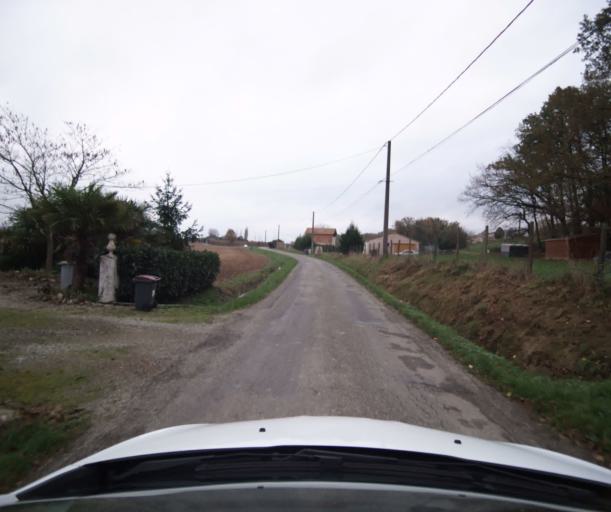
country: FR
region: Midi-Pyrenees
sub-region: Departement du Tarn-et-Garonne
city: Moissac
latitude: 44.0799
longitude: 1.1454
